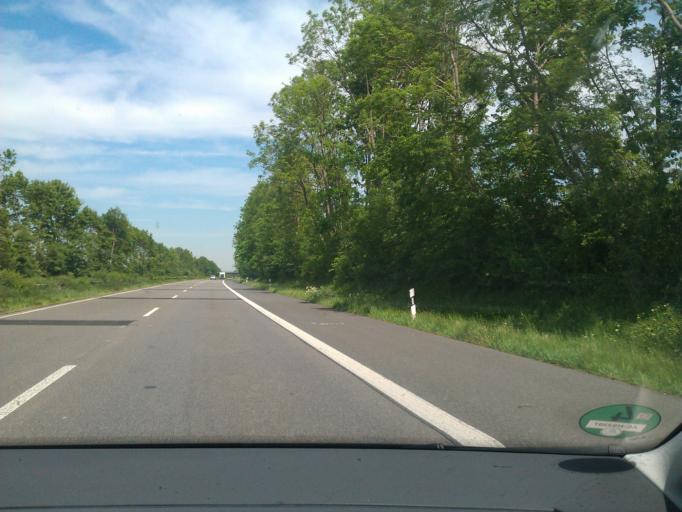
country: DE
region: North Rhine-Westphalia
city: Julich
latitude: 50.9516
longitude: 6.3504
